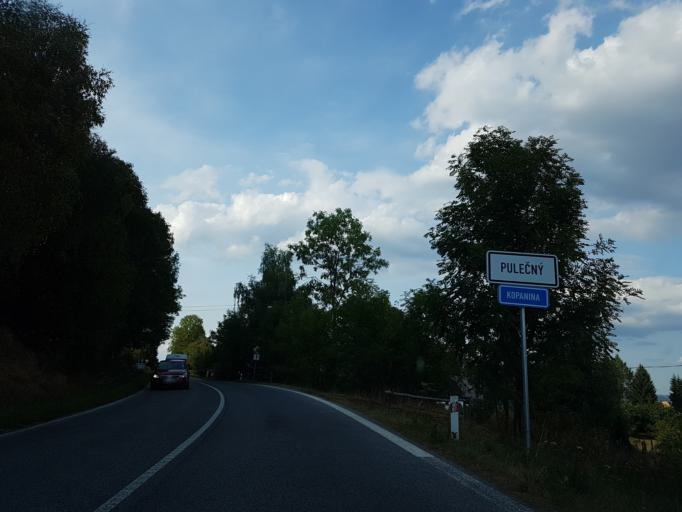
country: CZ
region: Liberecky
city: Mala Skala
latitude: 50.6607
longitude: 15.1680
